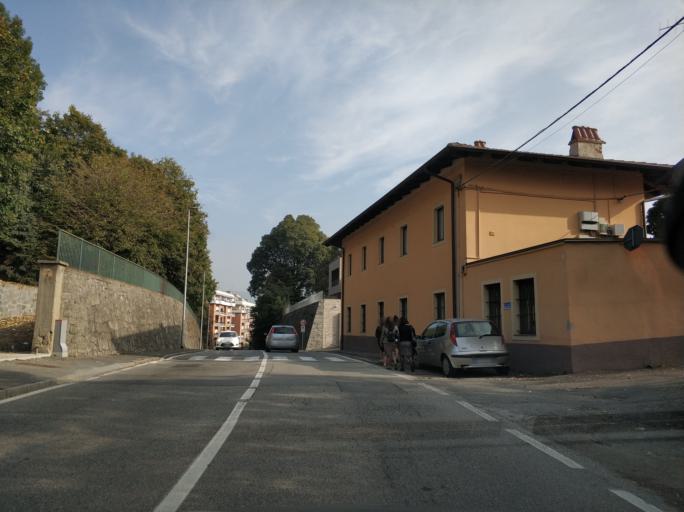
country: IT
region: Piedmont
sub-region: Provincia di Torino
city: Ivrea
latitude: 45.4608
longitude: 7.8696
